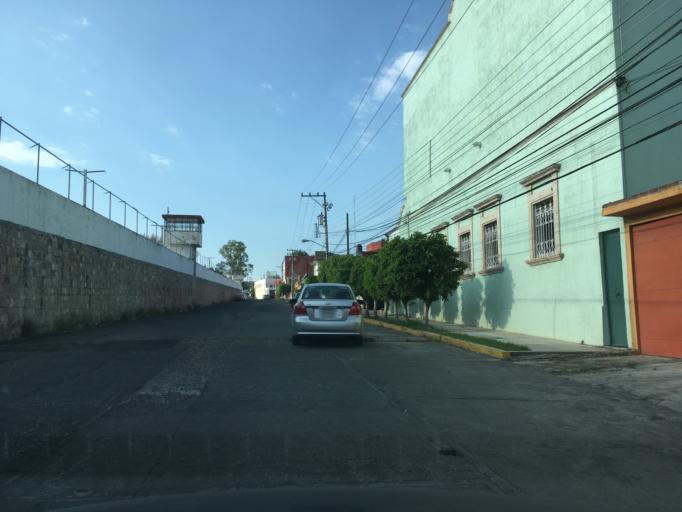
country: MX
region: Michoacan
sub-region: Morelia
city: Puerto de Buenavista (Lazaro Cardenas)
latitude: 19.6927
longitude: -101.1514
